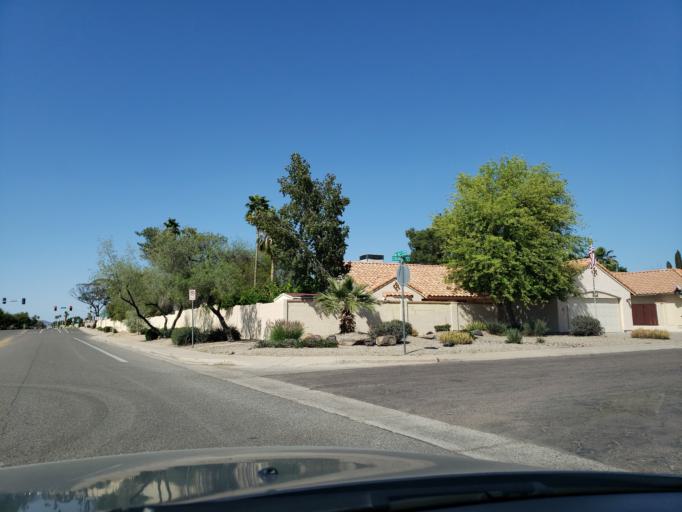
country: US
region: Arizona
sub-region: Maricopa County
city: Glendale
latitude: 33.5805
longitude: -112.1775
